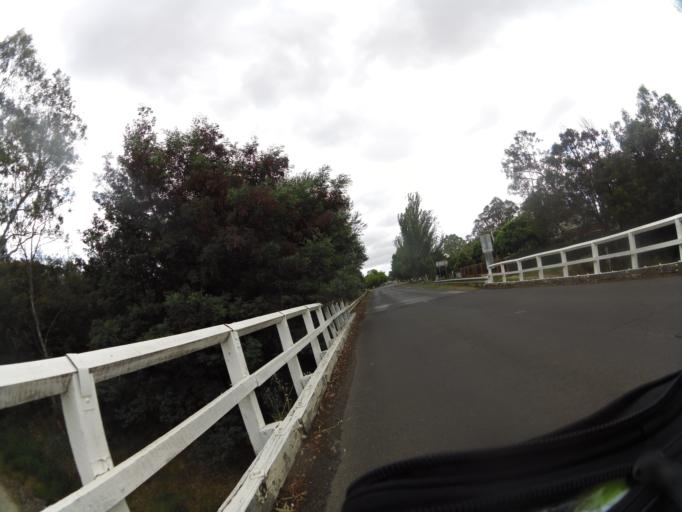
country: AU
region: Victoria
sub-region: Mount Alexander
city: Castlemaine
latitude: -37.0696
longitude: 144.2119
